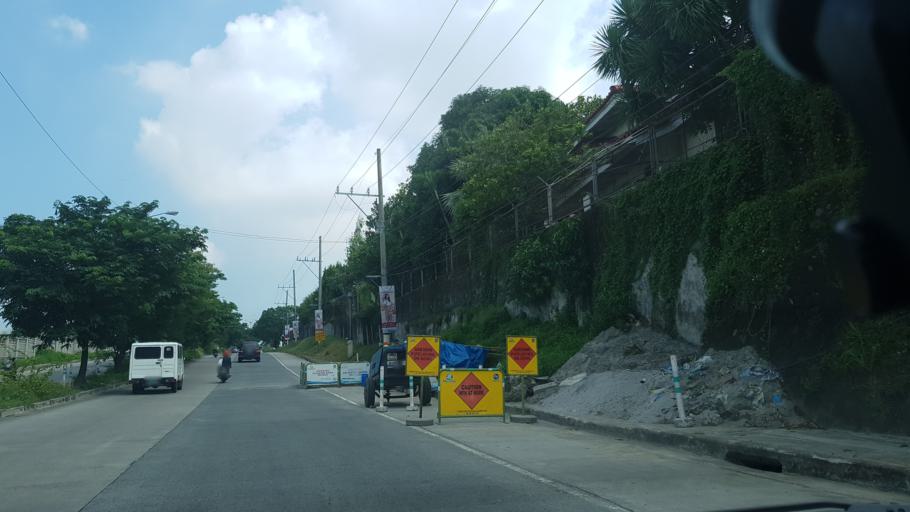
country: PH
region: Calabarzon
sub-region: Province of Laguna
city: San Pedro
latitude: 14.3898
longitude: 121.0096
